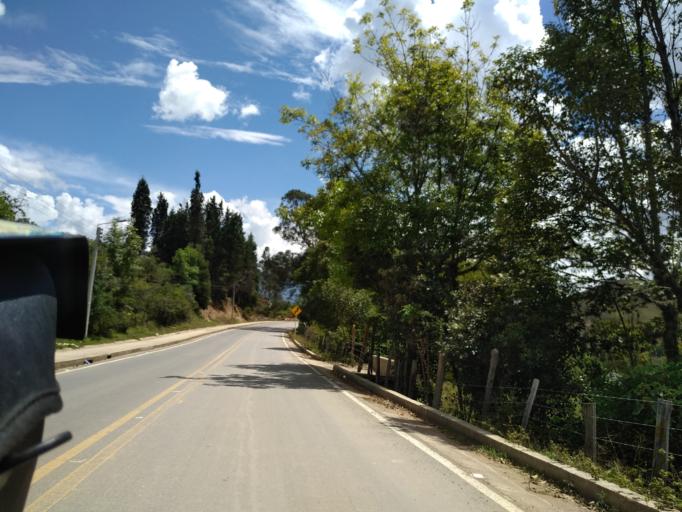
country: CO
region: Boyaca
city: Raquira
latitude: 5.5405
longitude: -73.6351
